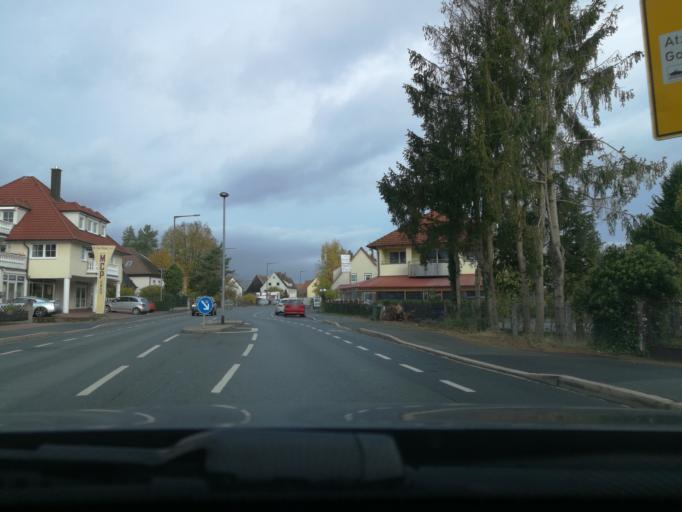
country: DE
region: Bavaria
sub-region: Regierungsbezirk Mittelfranken
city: Furth
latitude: 49.5093
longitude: 10.9760
